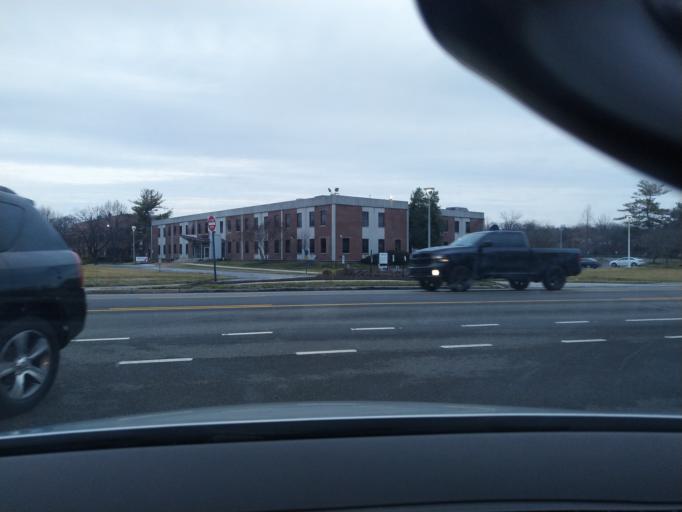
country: US
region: Pennsylvania
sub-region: Montgomery County
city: King of Prussia
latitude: 40.0951
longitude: -75.4046
